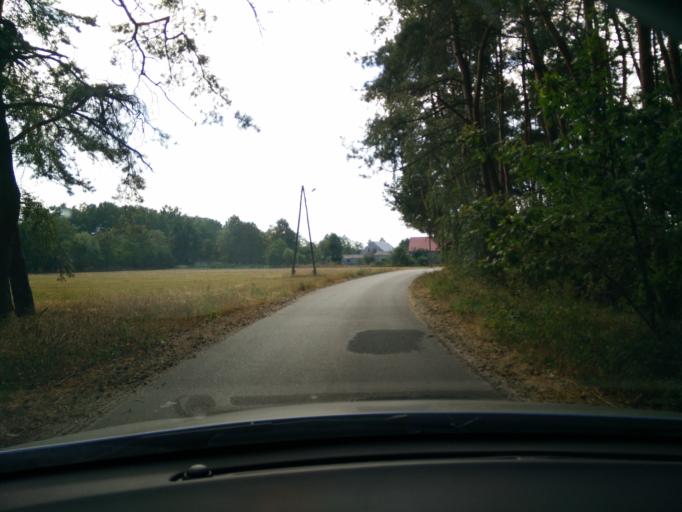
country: PL
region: Greater Poland Voivodeship
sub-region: Powiat poznanski
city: Kleszczewo
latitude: 52.2917
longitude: 17.2341
